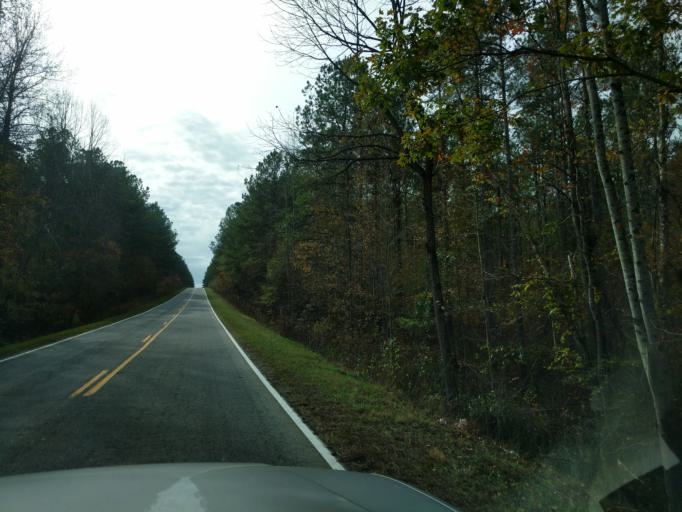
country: US
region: South Carolina
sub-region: Greenwood County
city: Ninety Six
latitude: 34.2264
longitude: -81.8769
